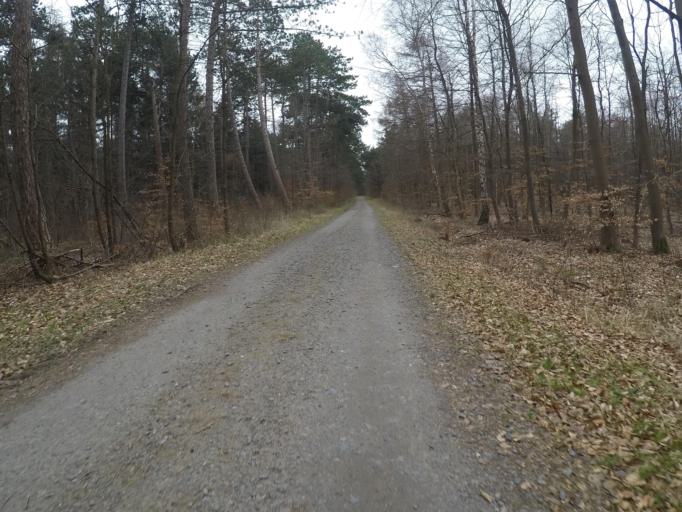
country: DE
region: Lower Saxony
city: Nordholz
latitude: 53.8185
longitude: 8.6379
